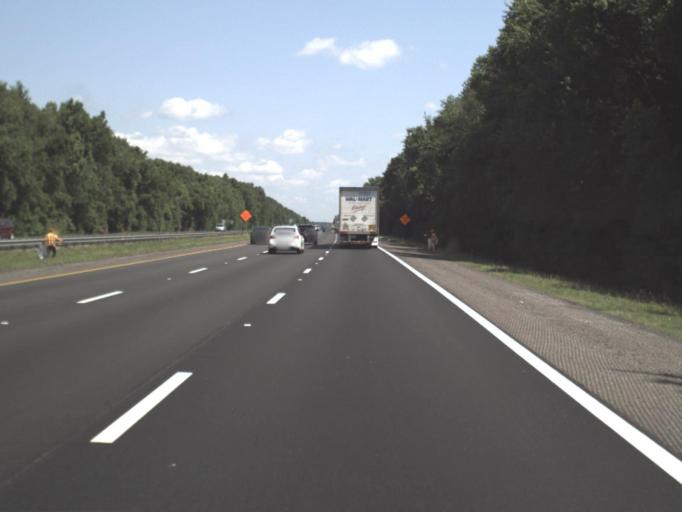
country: US
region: Florida
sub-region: Nassau County
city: Yulee
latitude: 30.5451
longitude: -81.6382
